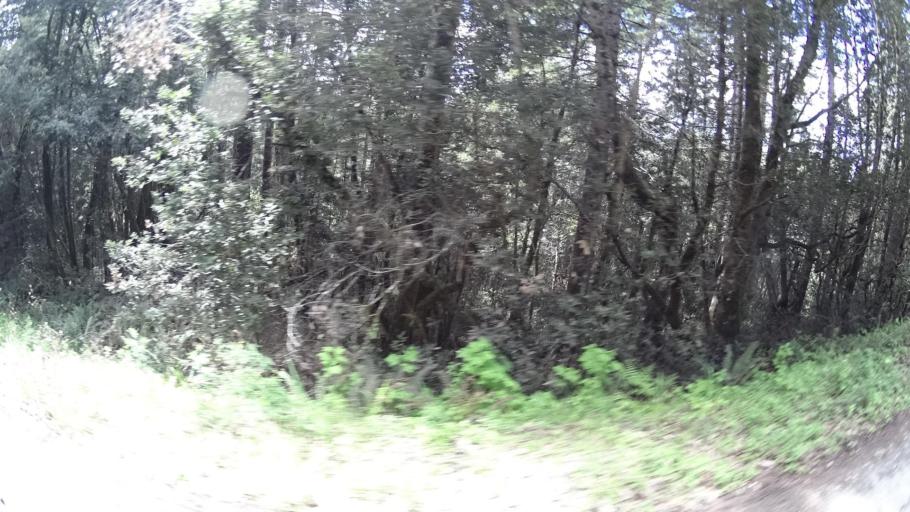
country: US
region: California
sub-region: Humboldt County
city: Blue Lake
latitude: 40.7963
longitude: -123.8753
